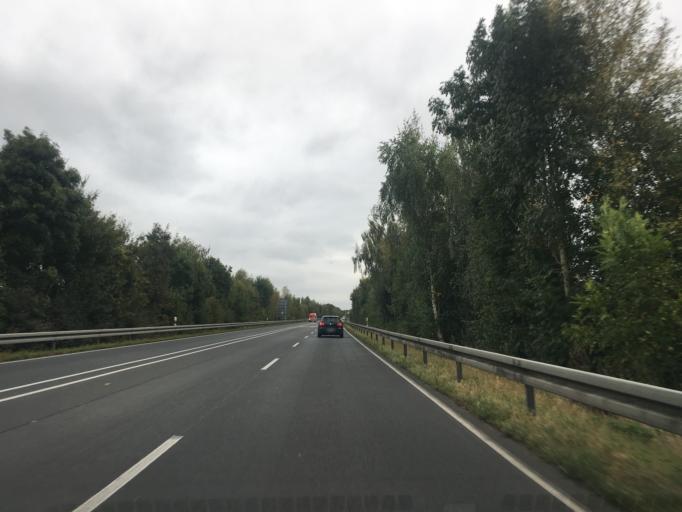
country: DE
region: North Rhine-Westphalia
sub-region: Regierungsbezirk Munster
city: Metelen
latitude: 52.1846
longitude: 7.2365
